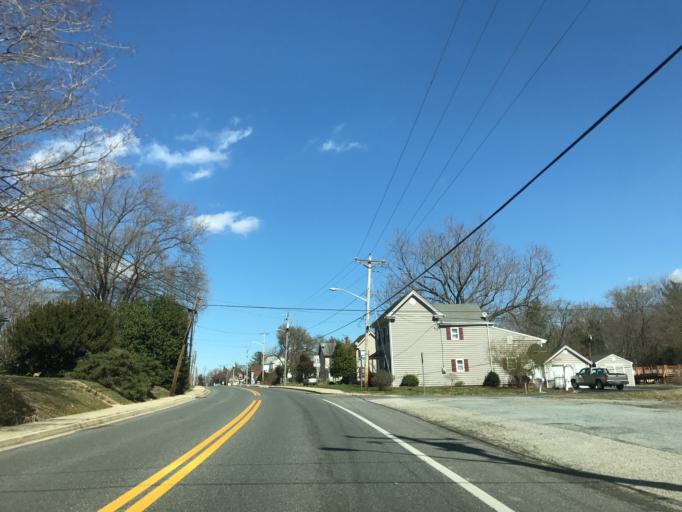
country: US
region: Maryland
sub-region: Queen Anne's County
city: Kingstown
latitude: 39.1455
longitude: -75.9810
